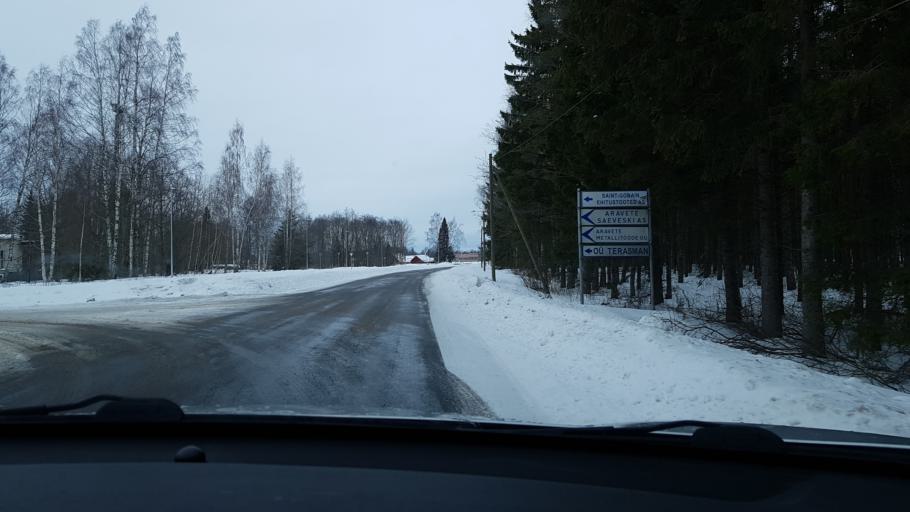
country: EE
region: Jaervamaa
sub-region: Jaerva-Jaani vald
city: Jarva-Jaani
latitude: 59.1309
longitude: 25.7437
